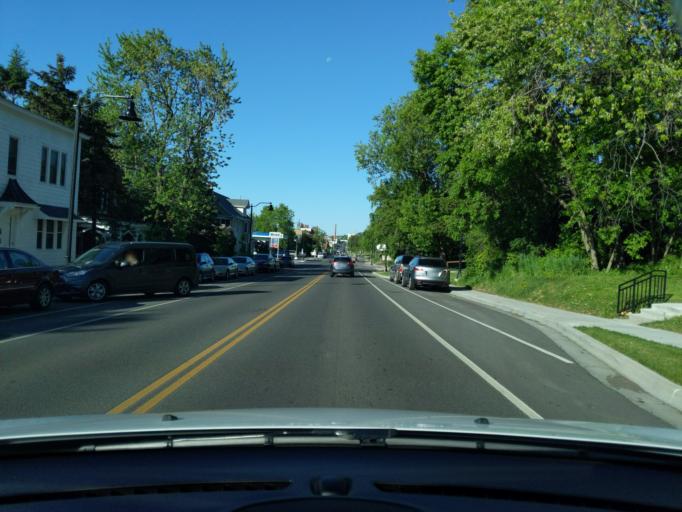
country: US
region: Minnesota
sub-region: Saint Louis County
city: Duluth
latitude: 46.8018
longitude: -92.0868
